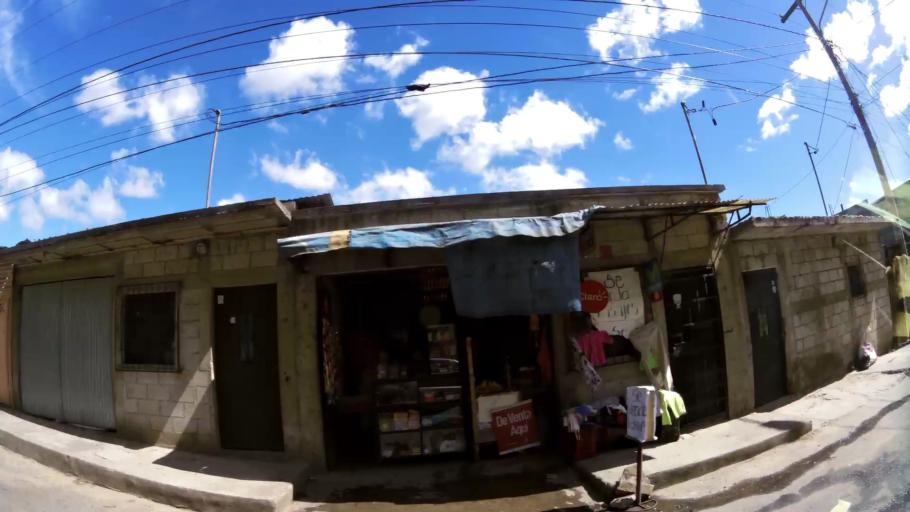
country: GT
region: Guatemala
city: Petapa
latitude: 14.5450
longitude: -90.5485
